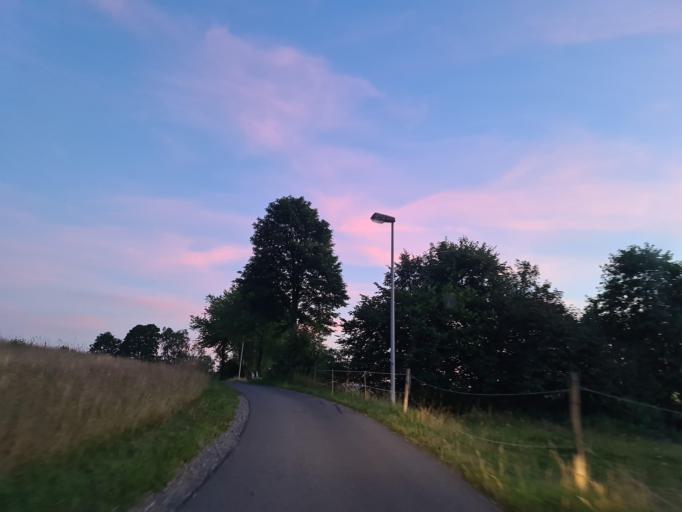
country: DE
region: Saxony
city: Neuhausen
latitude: 50.6863
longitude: 13.4838
